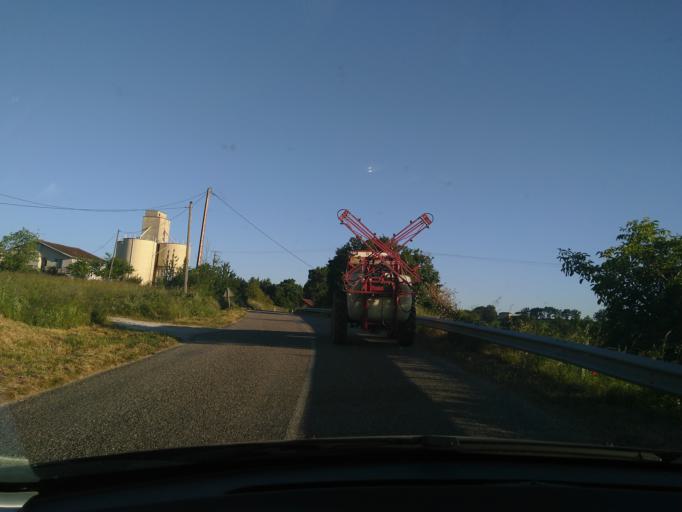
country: FR
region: Midi-Pyrenees
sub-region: Departement du Gers
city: Jegun
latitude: 43.8562
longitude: 0.5225
